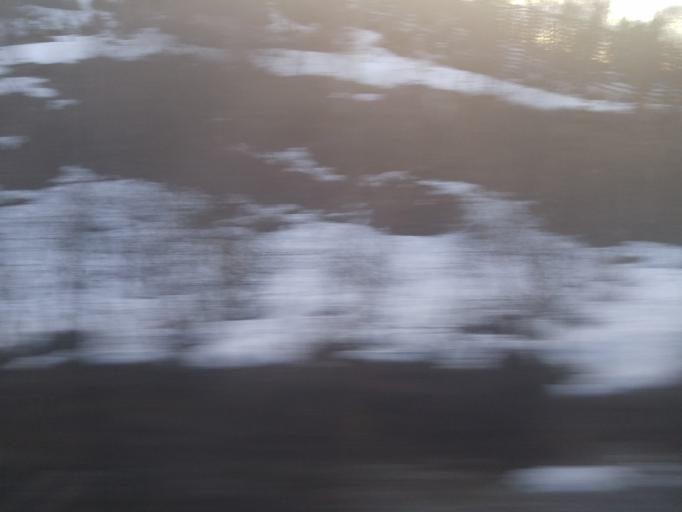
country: NO
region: Sor-Trondelag
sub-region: Oppdal
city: Oppdal
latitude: 62.2844
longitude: 9.5955
